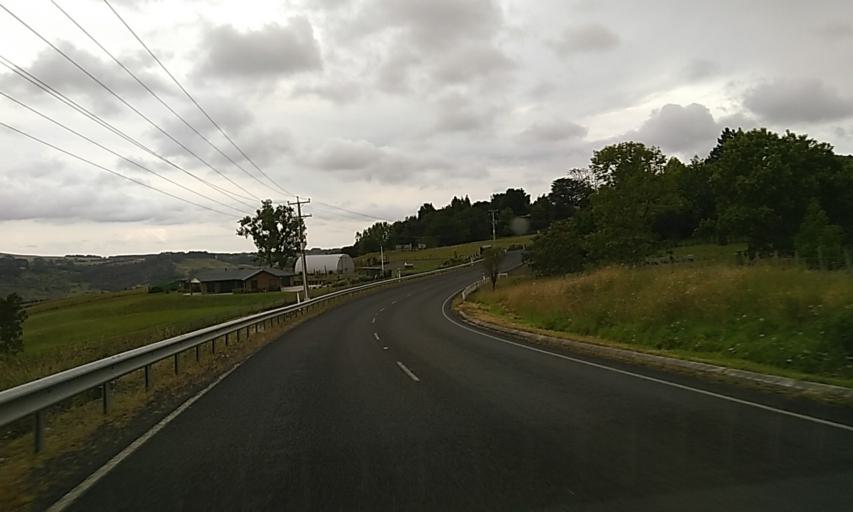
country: NZ
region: Auckland
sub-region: Auckland
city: Pukekohe East
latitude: -37.3110
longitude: 174.9379
